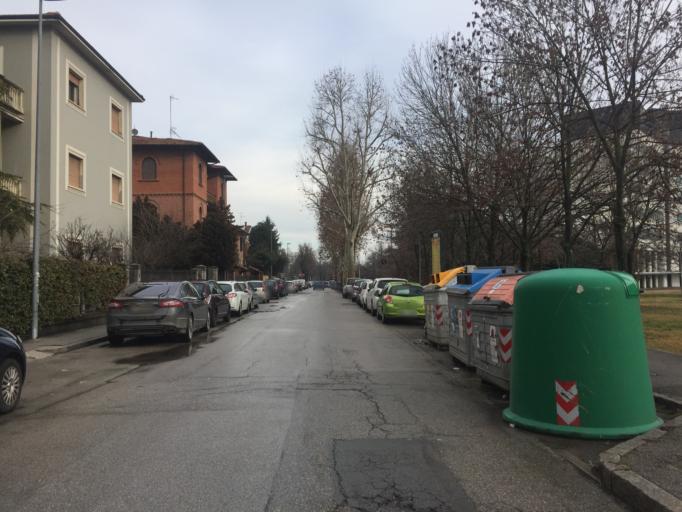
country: IT
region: Emilia-Romagna
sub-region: Provincia di Bologna
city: Bologna
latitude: 44.5083
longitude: 11.3037
